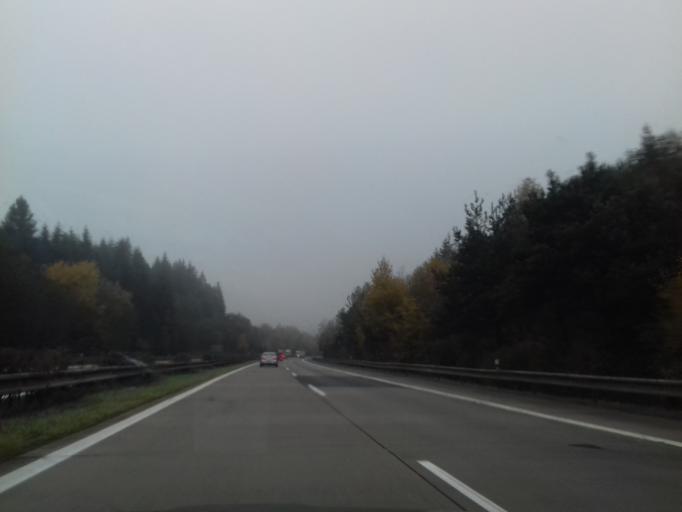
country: CZ
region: Vysocina
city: Heralec
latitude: 49.4932
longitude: 15.4907
